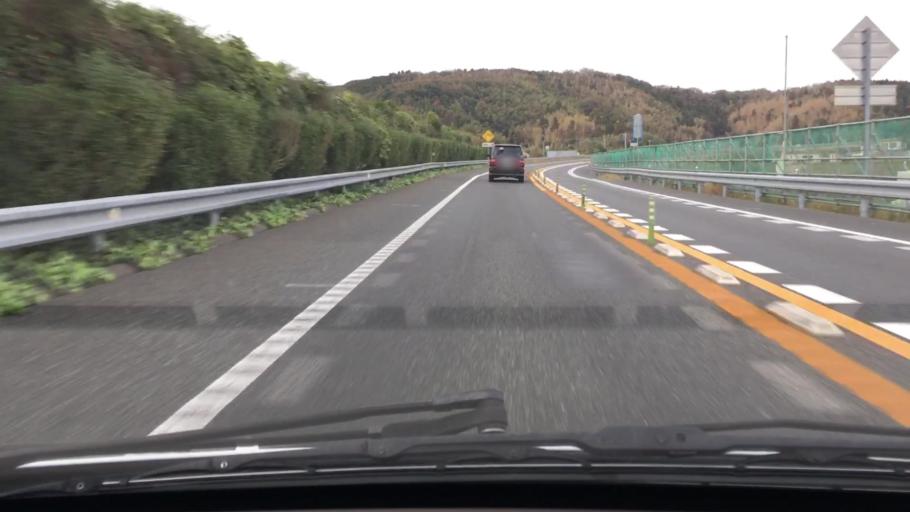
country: JP
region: Chiba
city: Kimitsu
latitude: 35.2202
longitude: 139.8850
